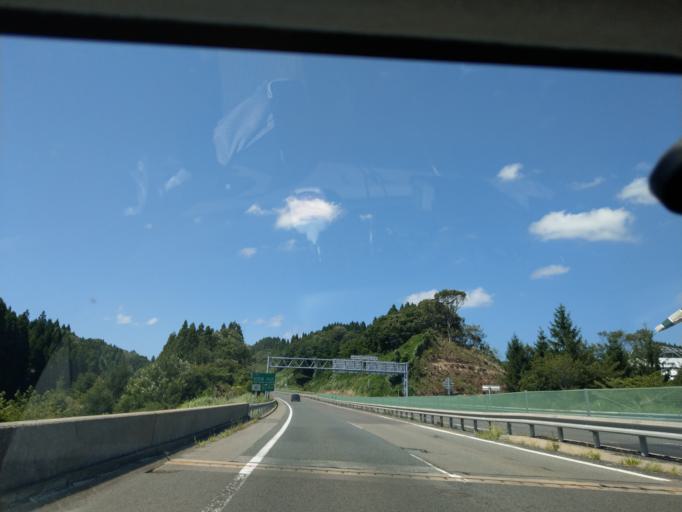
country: JP
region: Akita
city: Akita
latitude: 39.6521
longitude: 140.2047
